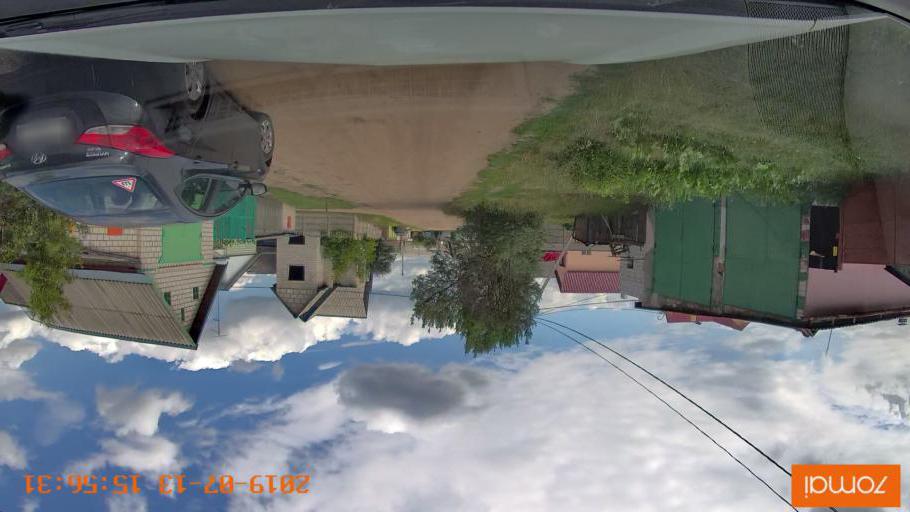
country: BY
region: Mogilev
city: Babruysk
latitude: 53.1434
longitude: 29.2022
